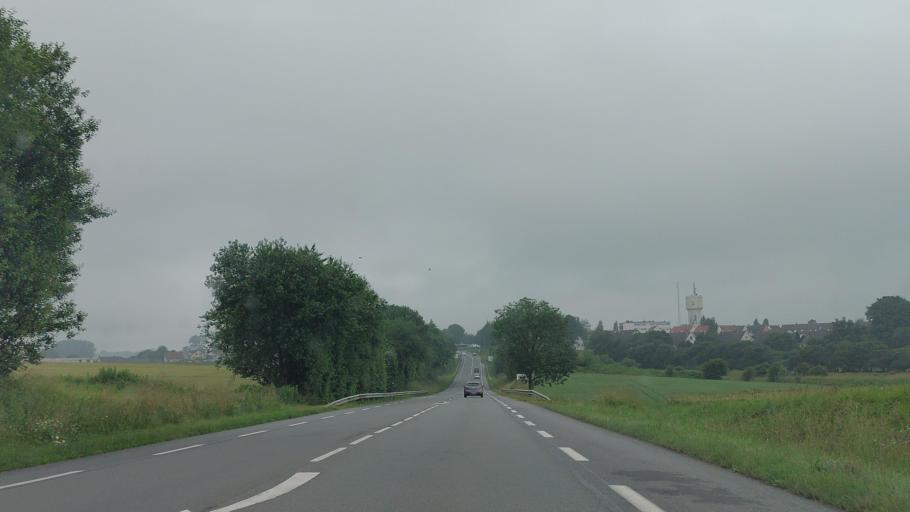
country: FR
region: Picardie
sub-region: Departement de la Somme
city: Friville-Escarbotin
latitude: 50.0733
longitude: 1.5512
